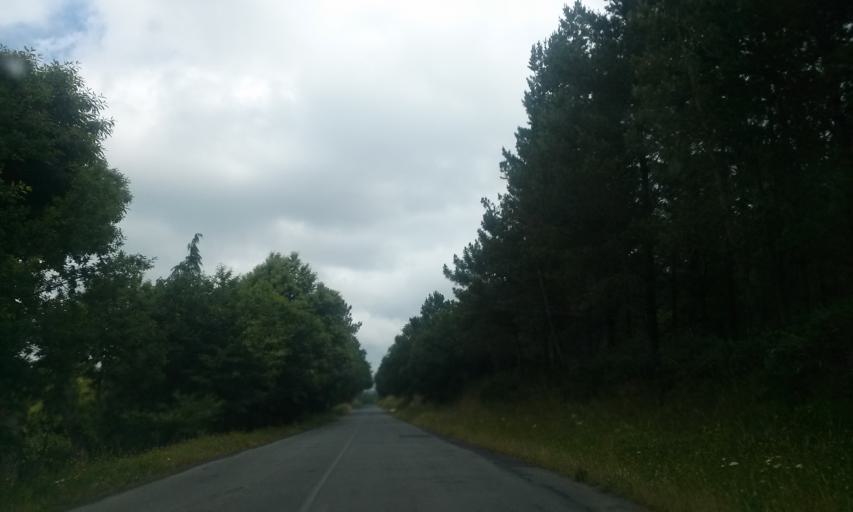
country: ES
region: Galicia
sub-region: Provincia de Lugo
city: Friol
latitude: 43.0829
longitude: -7.8146
